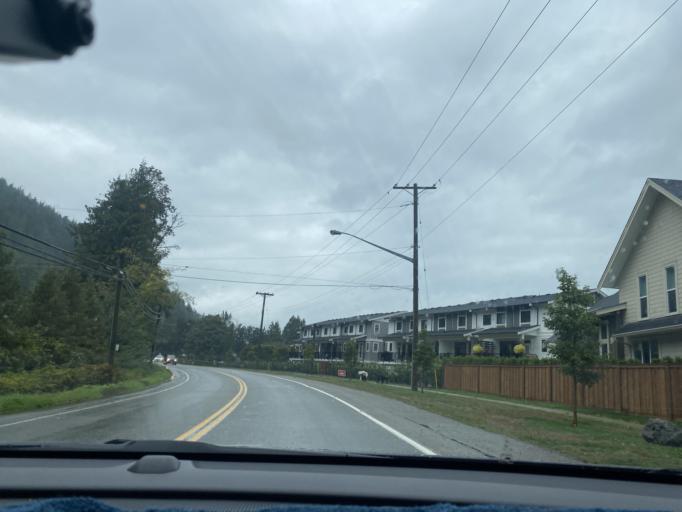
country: CA
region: British Columbia
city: Agassiz
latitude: 49.2928
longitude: -121.7809
